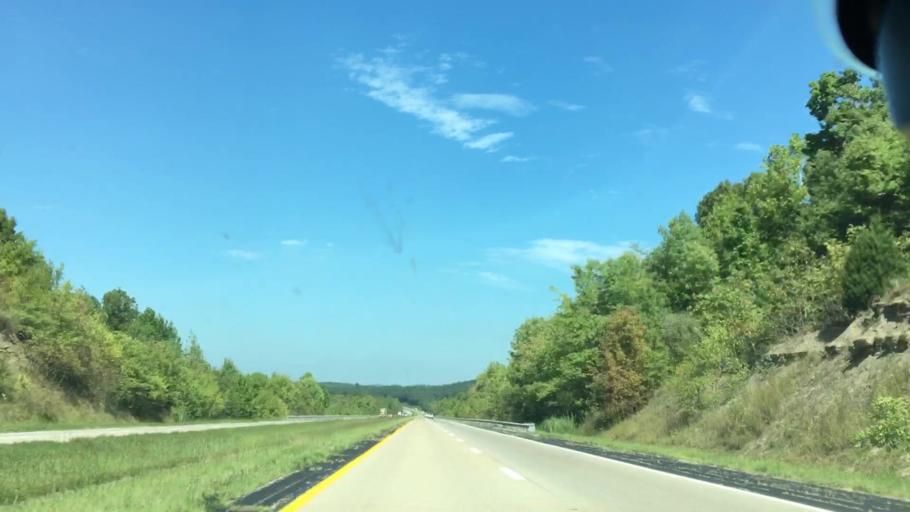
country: US
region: Kentucky
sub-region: Hopkins County
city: Nortonville
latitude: 37.1144
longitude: -87.4585
